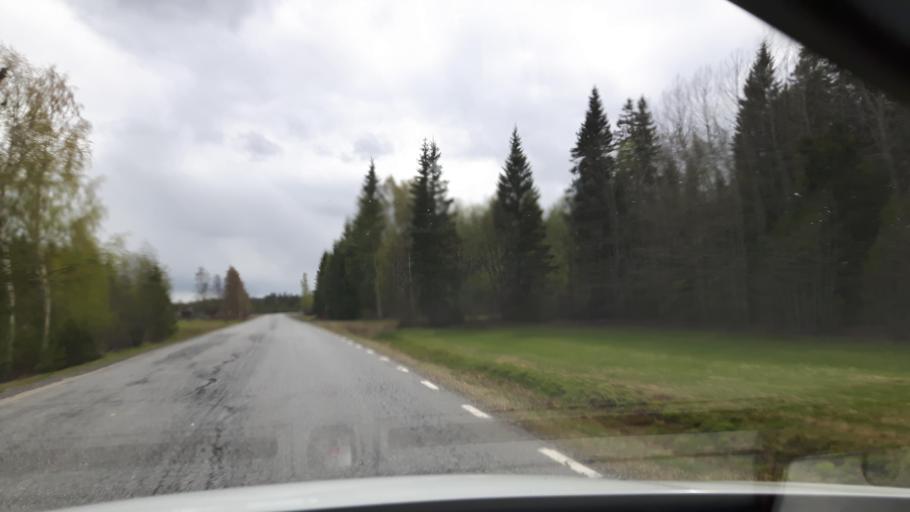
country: SE
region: Vaesterbotten
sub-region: Skelleftea Kommun
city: Burtraesk
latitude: 64.3146
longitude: 20.5315
